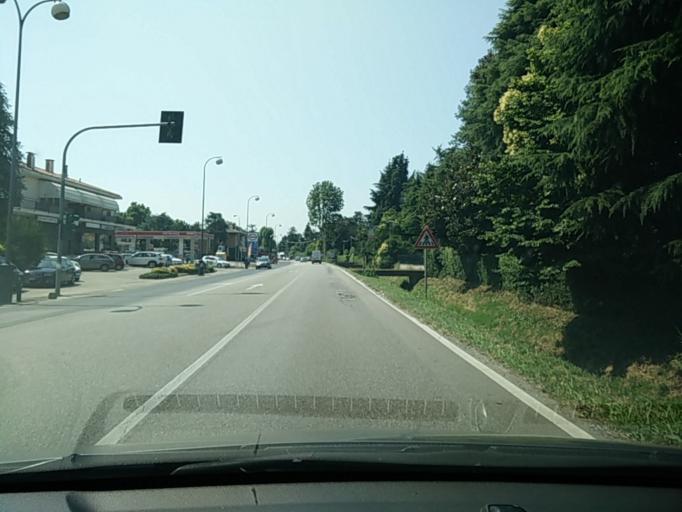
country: IT
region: Veneto
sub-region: Provincia di Treviso
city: Mogliano Veneto
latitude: 45.5560
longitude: 12.2343
